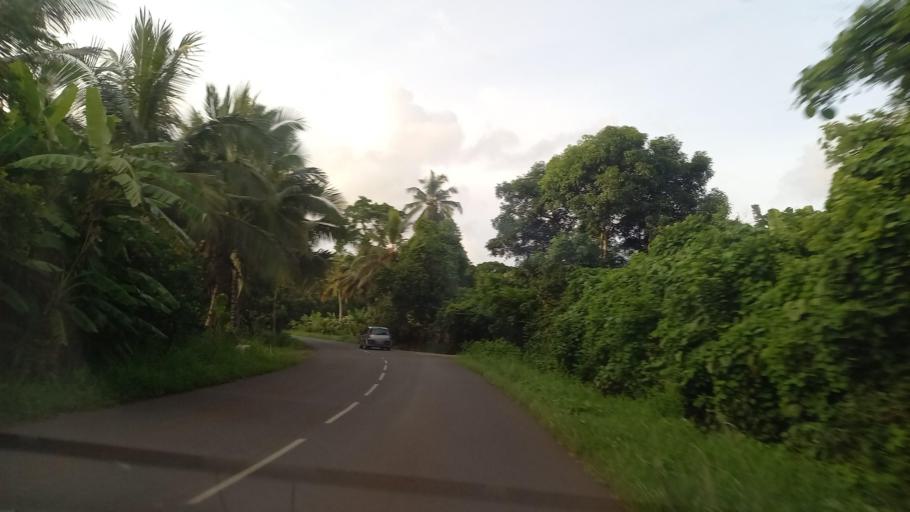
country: YT
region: M'Tsangamouji
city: M'Tsangamouji
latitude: -12.7625
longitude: 45.1042
